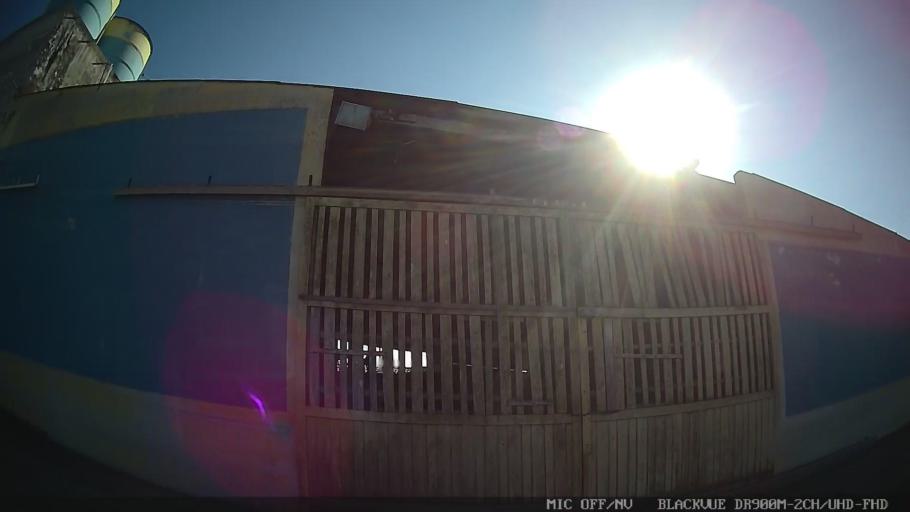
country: BR
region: Sao Paulo
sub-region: Peruibe
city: Peruibe
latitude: -24.2758
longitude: -46.9522
